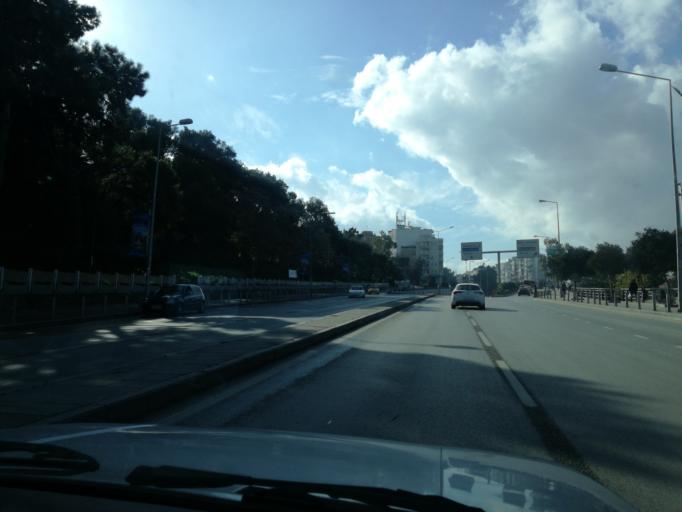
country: TR
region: Izmir
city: Izmir
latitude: 38.4122
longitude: 27.1311
